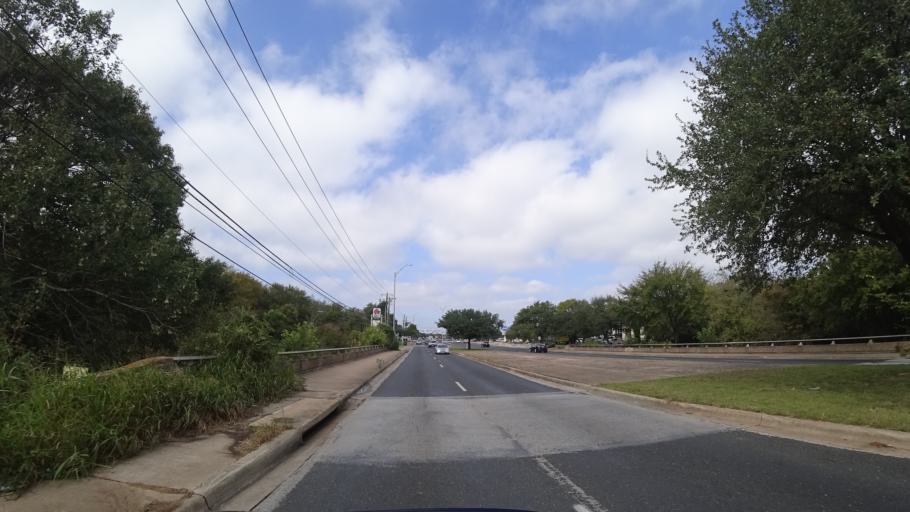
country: US
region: Texas
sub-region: Travis County
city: Shady Hollow
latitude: 30.2128
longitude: -97.8285
